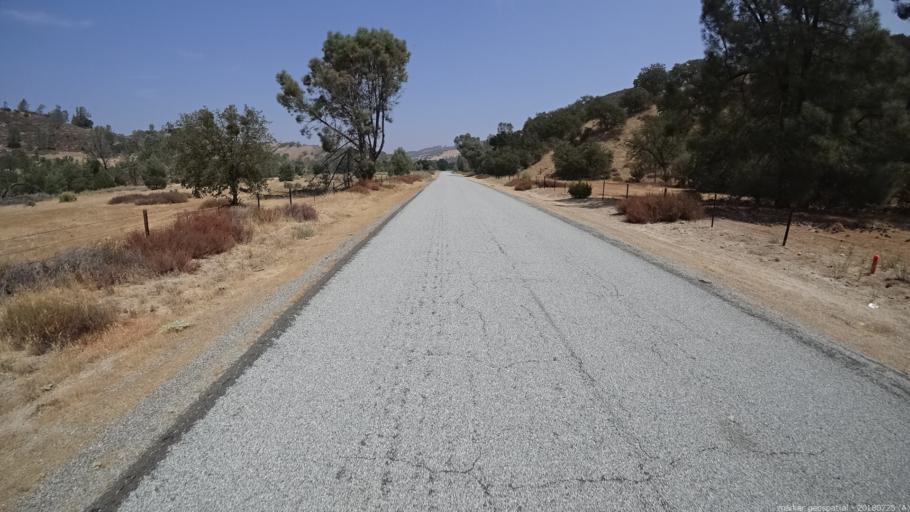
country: US
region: California
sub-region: San Luis Obispo County
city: San Miguel
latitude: 35.8588
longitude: -120.5865
